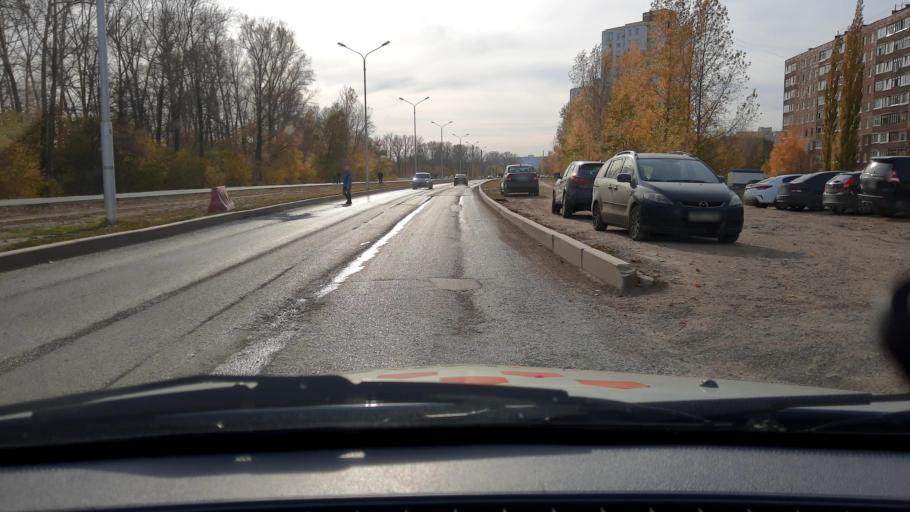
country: RU
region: Bashkortostan
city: Ufa
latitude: 54.7670
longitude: 56.0808
